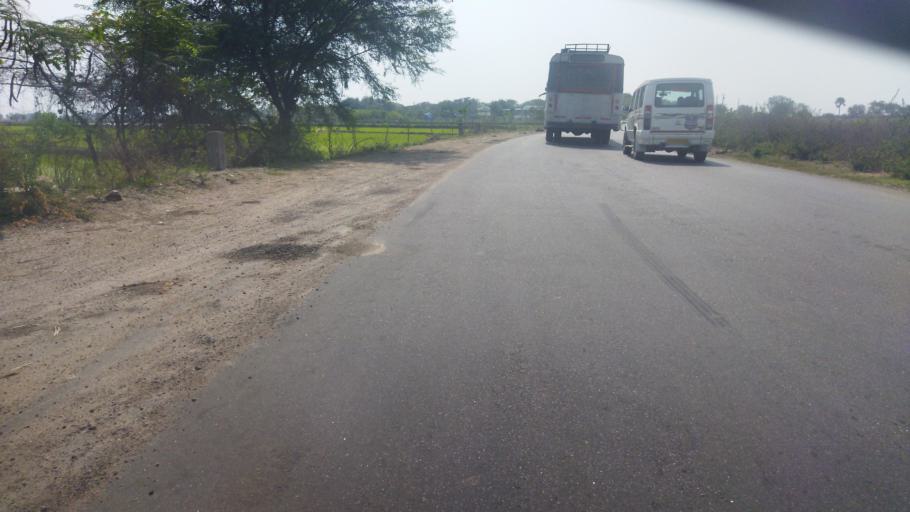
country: IN
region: Telangana
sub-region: Nalgonda
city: Nalgonda
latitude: 17.0982
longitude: 79.2857
